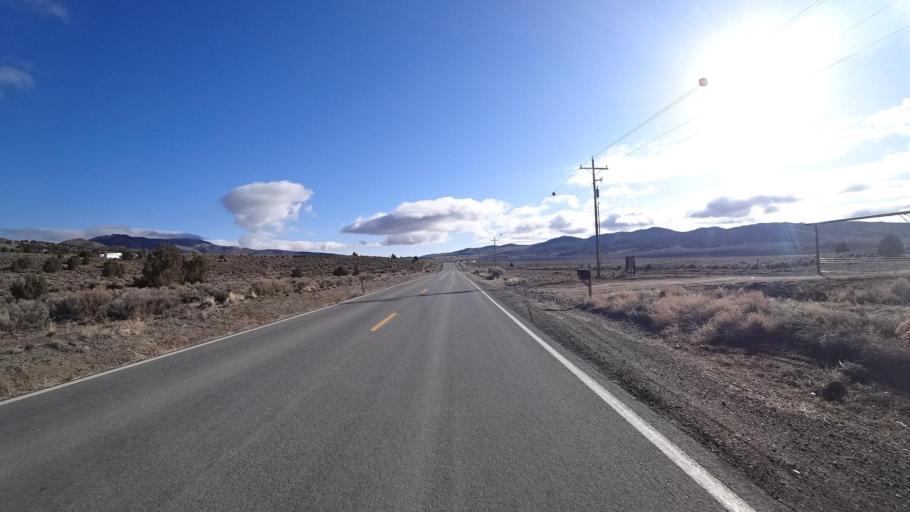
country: US
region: Nevada
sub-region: Washoe County
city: Lemmon Valley
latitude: 39.7183
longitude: -119.8873
